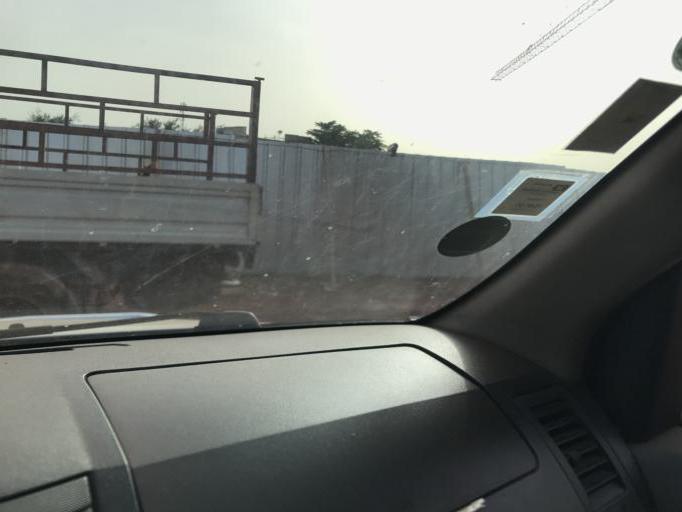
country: ML
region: Bamako
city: Bamako
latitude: 12.5876
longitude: -8.0053
